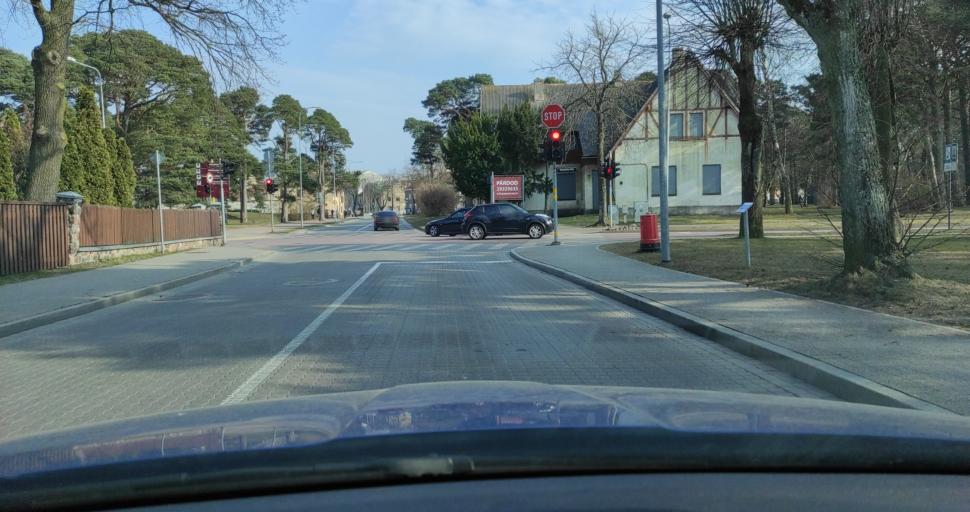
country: LV
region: Ventspils
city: Ventspils
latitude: 57.3905
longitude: 21.5466
